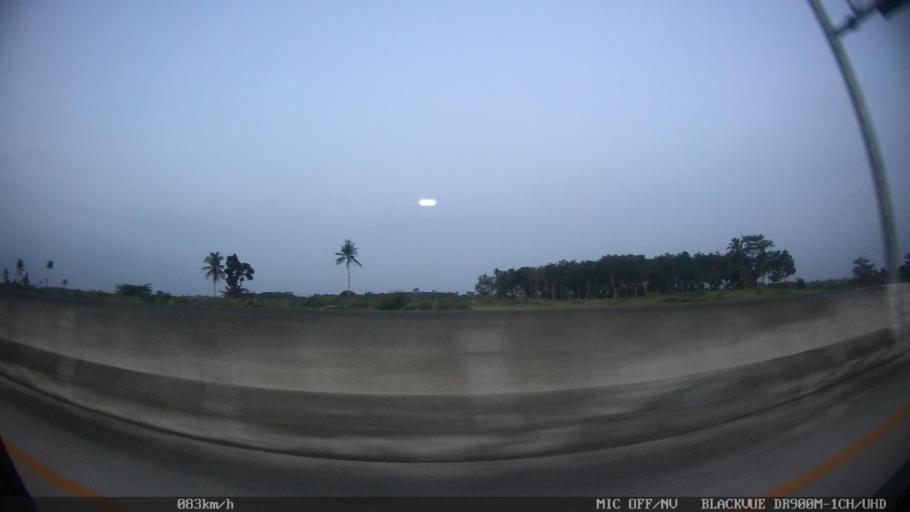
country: ID
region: Lampung
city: Sidorejo
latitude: -5.6194
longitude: 105.5620
